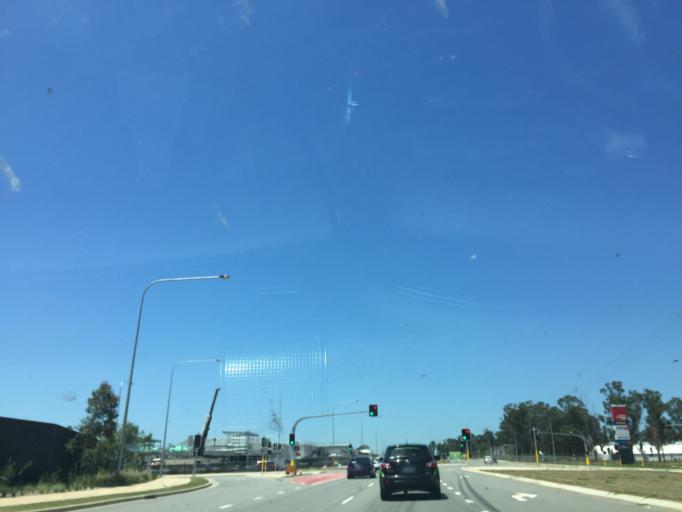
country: AU
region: New South Wales
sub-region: Blacktown
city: Hassall Grove
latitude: -33.7231
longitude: 150.8445
